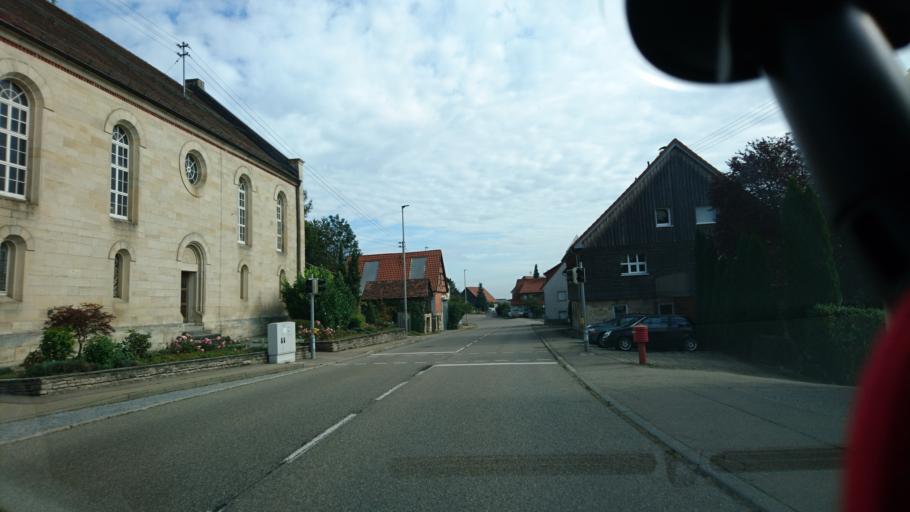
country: DE
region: Baden-Wuerttemberg
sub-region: Regierungsbezirk Stuttgart
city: Grosserlach
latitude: 49.0534
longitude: 9.5149
